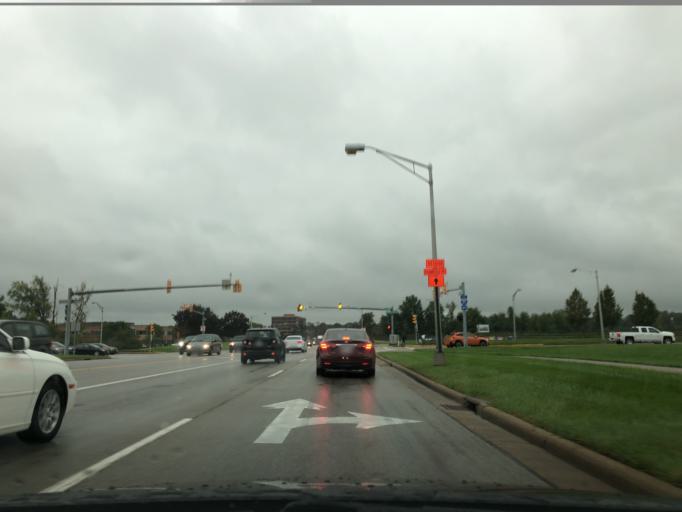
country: US
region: Ohio
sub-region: Hamilton County
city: Blue Ash
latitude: 39.2521
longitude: -84.3800
